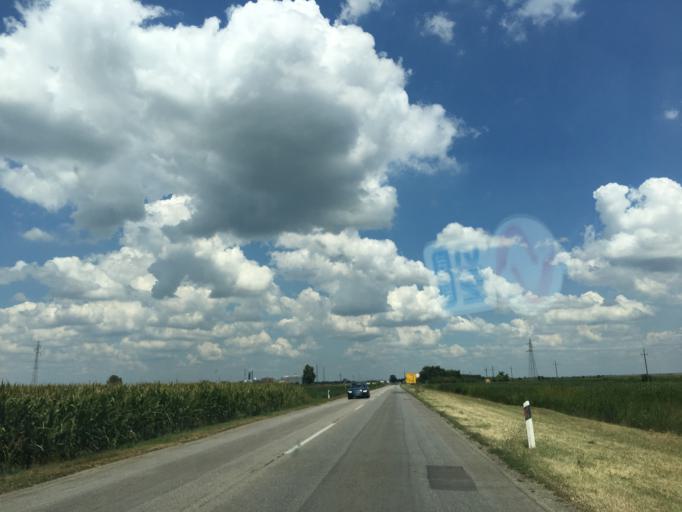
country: RS
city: Debeljaca
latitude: 45.0658
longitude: 20.6403
